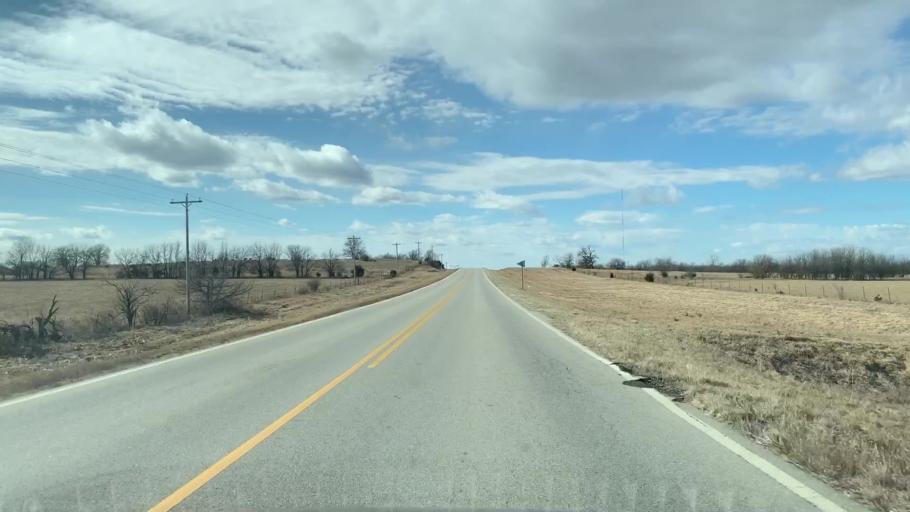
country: US
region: Kansas
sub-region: Neosho County
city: Erie
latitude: 37.5292
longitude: -95.3690
